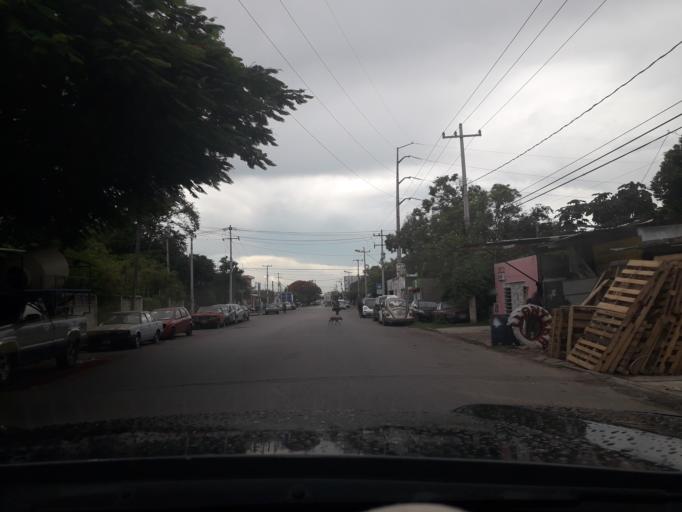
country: MX
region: Yucatan
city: Merida
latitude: 20.9567
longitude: -89.6480
